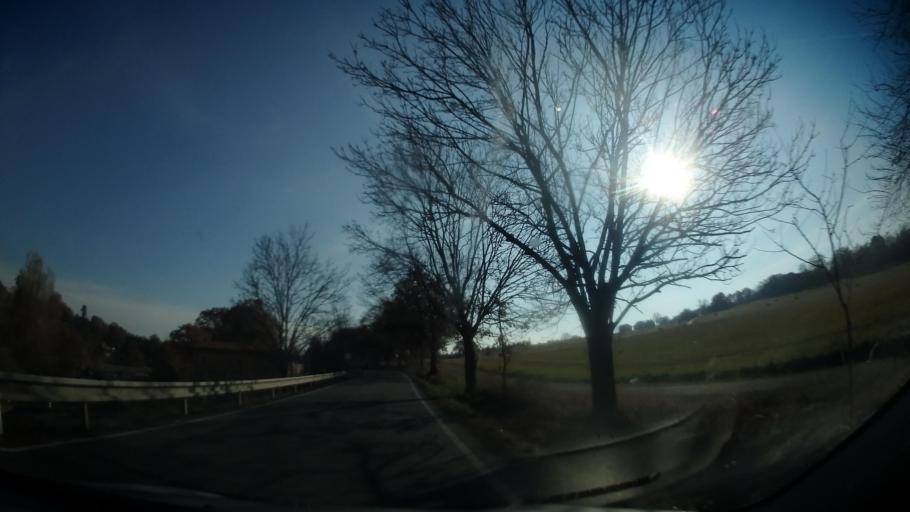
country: CZ
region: Central Bohemia
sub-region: Okres Praha-Vychod
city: Mnichovice
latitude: 49.9179
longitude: 14.7220
